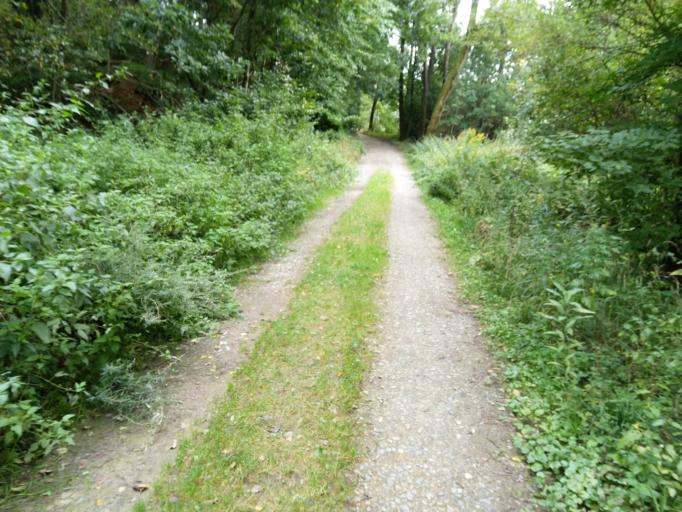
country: DE
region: North Rhine-Westphalia
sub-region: Regierungsbezirk Detmold
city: Bad Salzuflen
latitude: 52.0846
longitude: 8.7913
